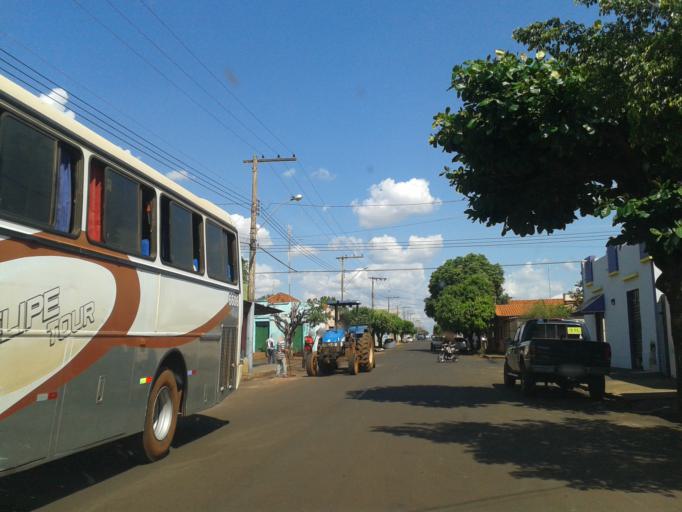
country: BR
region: Minas Gerais
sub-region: Centralina
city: Centralina
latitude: -18.7200
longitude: -49.2028
